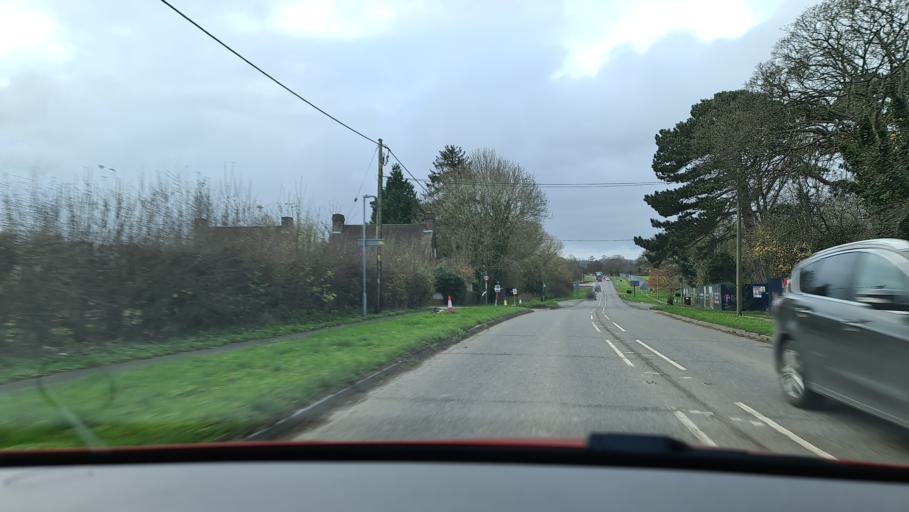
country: GB
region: England
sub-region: Buckinghamshire
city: Weston Turville
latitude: 51.7816
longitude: -0.7902
